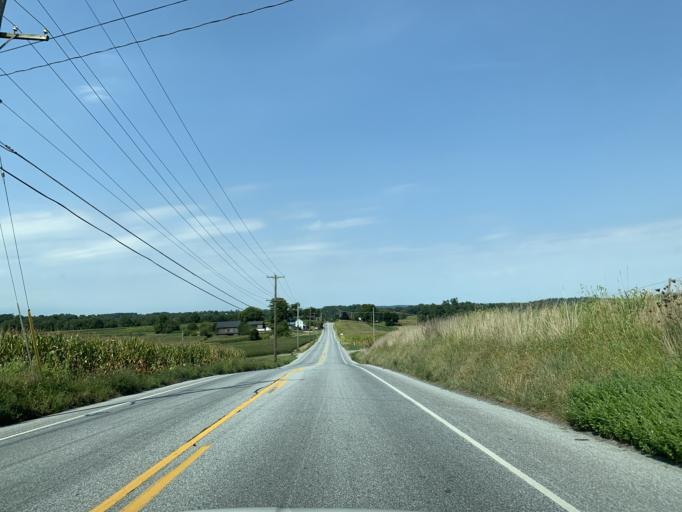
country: US
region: Pennsylvania
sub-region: York County
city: Susquehanna Trails
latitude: 39.7536
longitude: -76.3299
